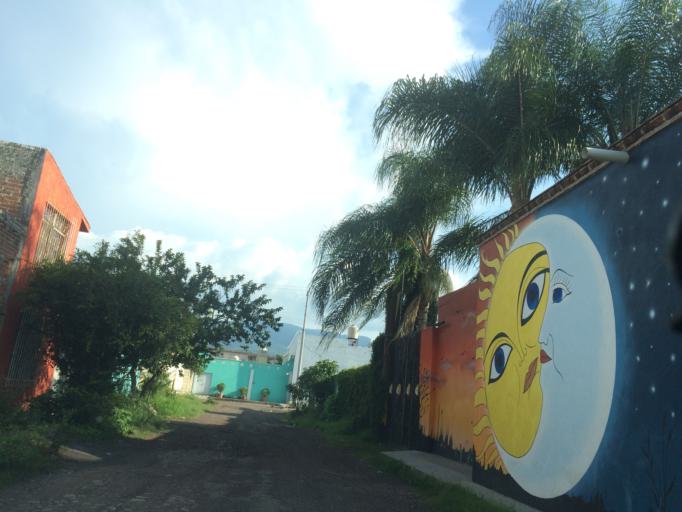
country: MX
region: Nayarit
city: Ixtlan del Rio
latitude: 21.0344
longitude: -104.3886
